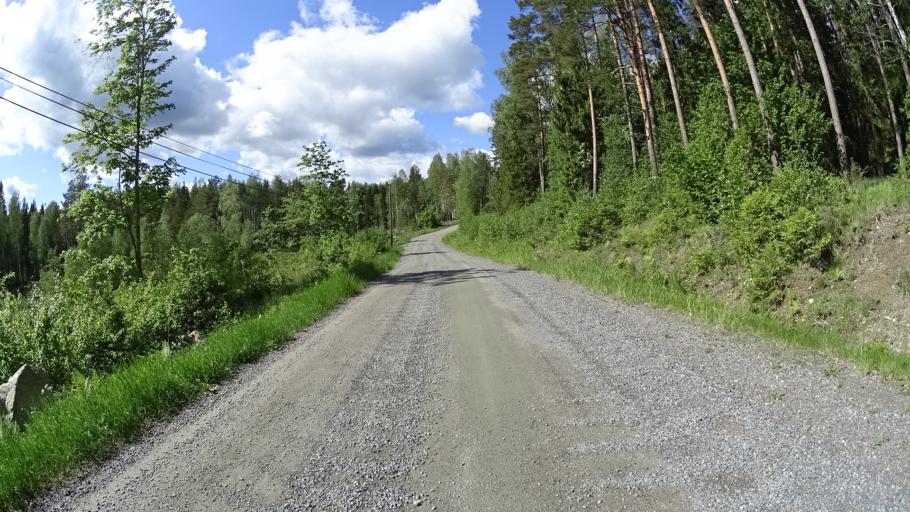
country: FI
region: Uusimaa
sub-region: Raaseporin
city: Pohja
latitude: 60.1738
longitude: 23.5860
